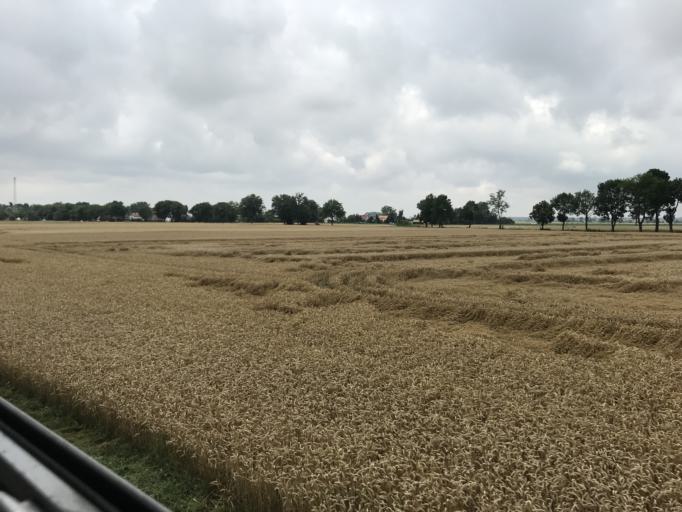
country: PL
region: Pomeranian Voivodeship
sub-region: Powiat malborski
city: Stare Pole
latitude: 54.0566
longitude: 19.2209
